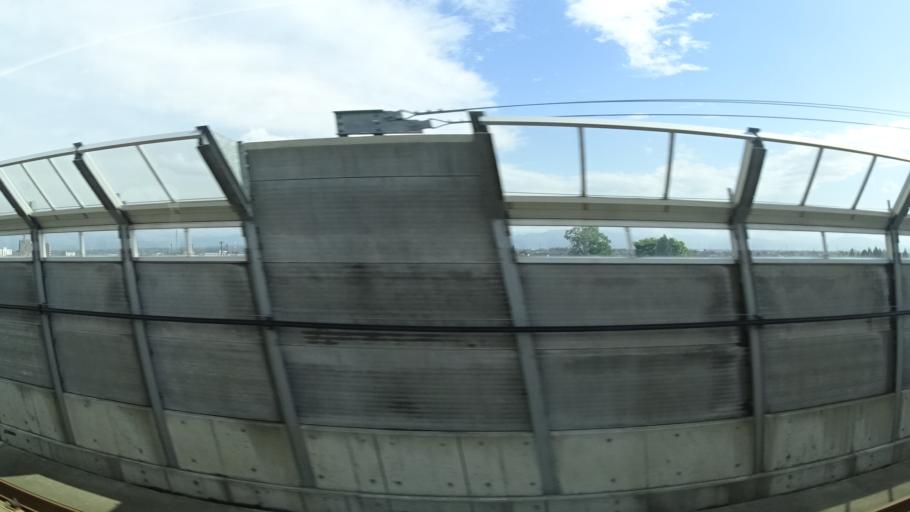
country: JP
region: Toyama
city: Takaoka
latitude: 36.7270
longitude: 137.0055
